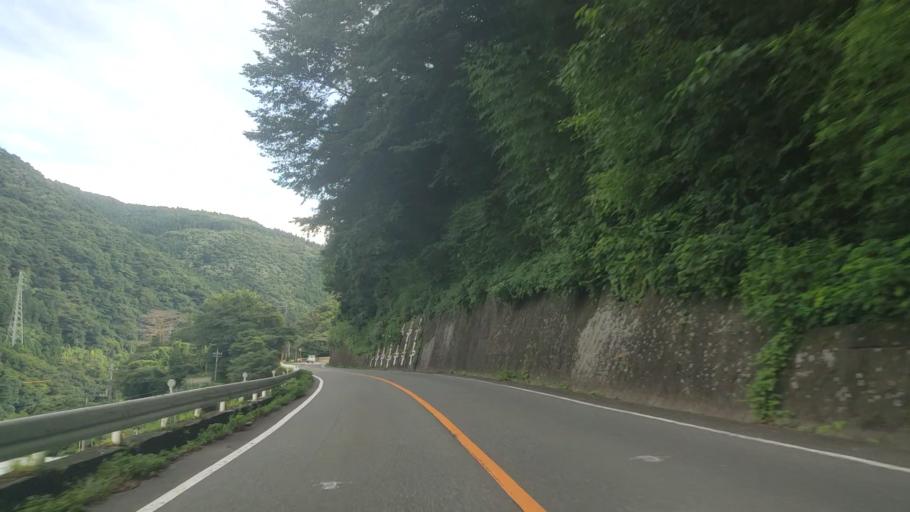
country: JP
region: Gunma
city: Omamacho-omama
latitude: 36.5098
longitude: 139.2958
